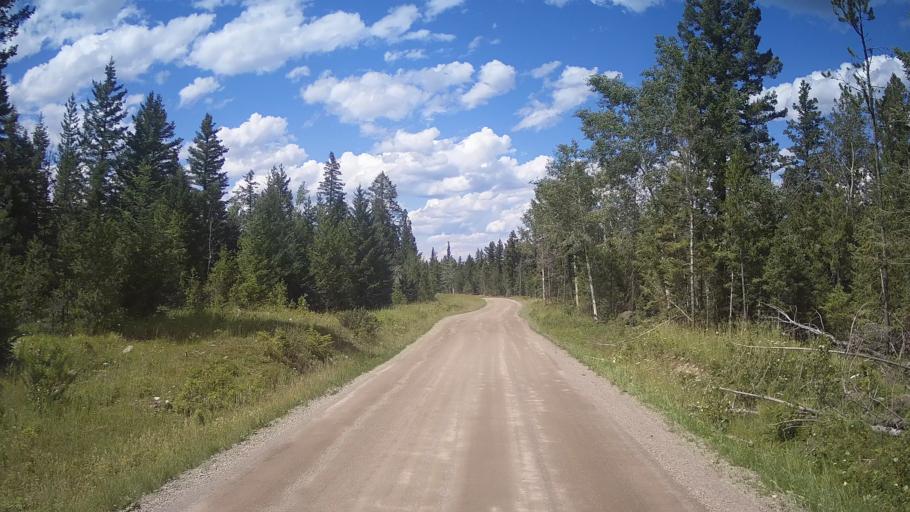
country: CA
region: British Columbia
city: Lillooet
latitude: 51.3146
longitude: -121.8568
